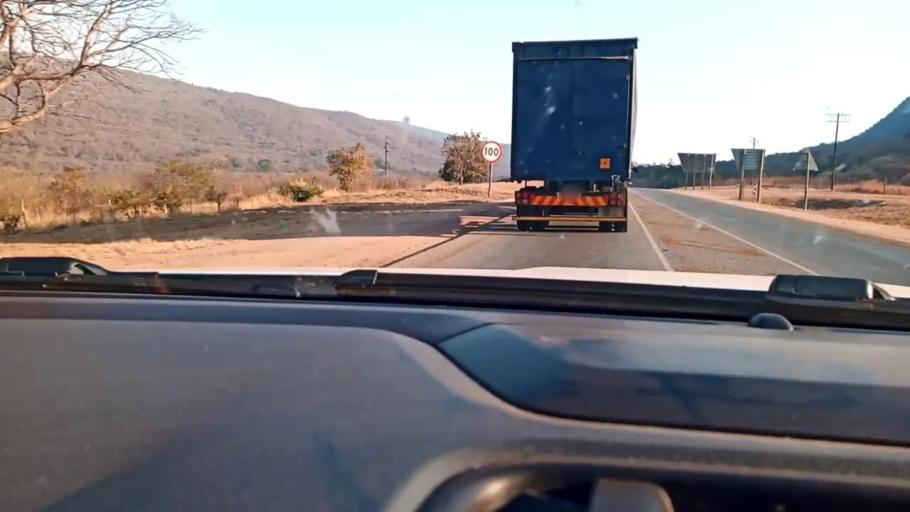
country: ZA
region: Limpopo
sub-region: Mopani District Municipality
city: Duiwelskloof
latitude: -23.6542
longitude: 30.1707
